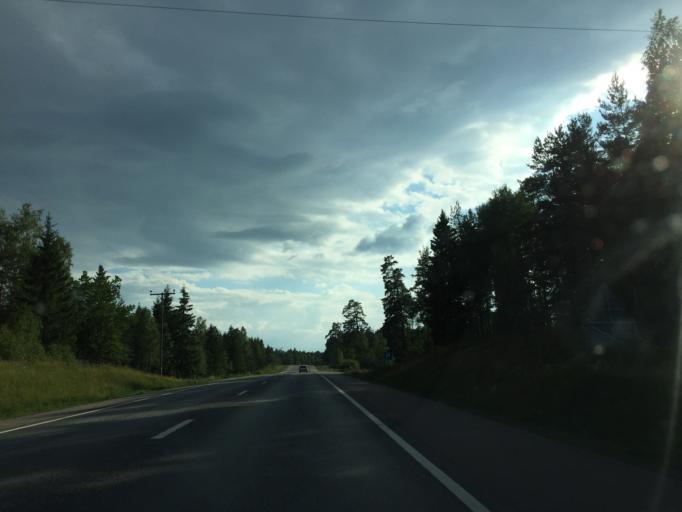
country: SE
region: Vaestmanland
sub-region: Arboga Kommun
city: Arboga
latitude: 59.3848
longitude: 15.8083
